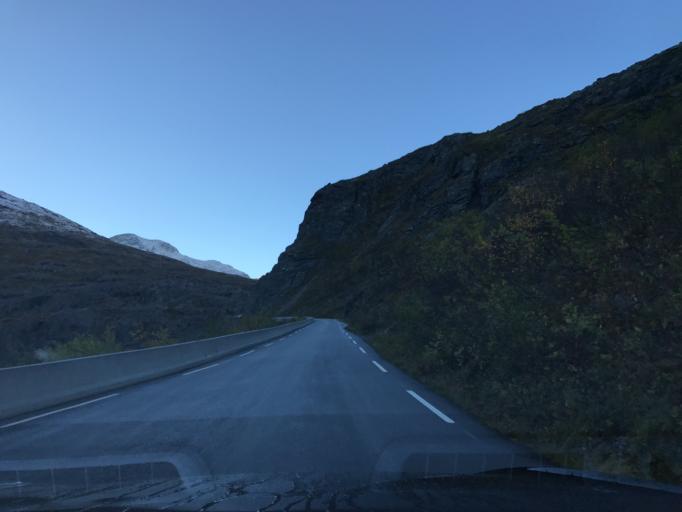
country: NO
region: More og Romsdal
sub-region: Rauma
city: Andalsnes
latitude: 62.4602
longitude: 7.6663
